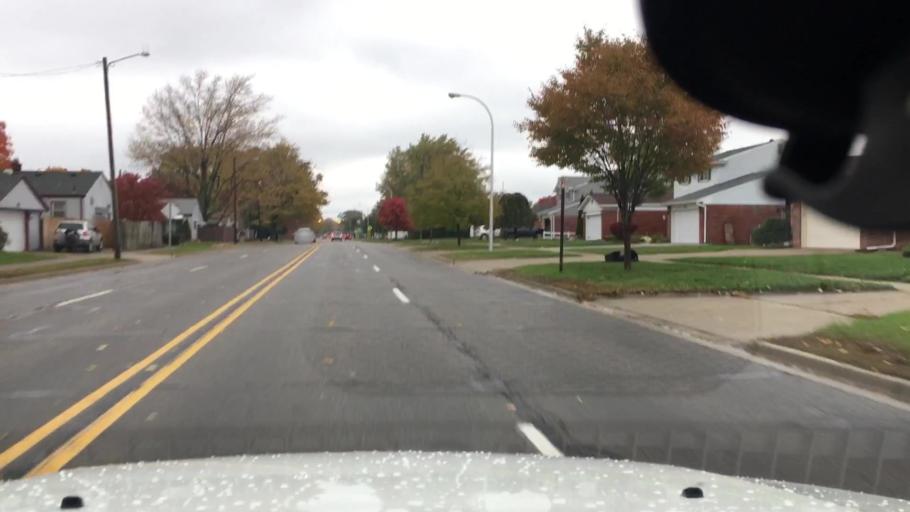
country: US
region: Michigan
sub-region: Oakland County
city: Clawson
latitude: 42.5251
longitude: -83.1259
